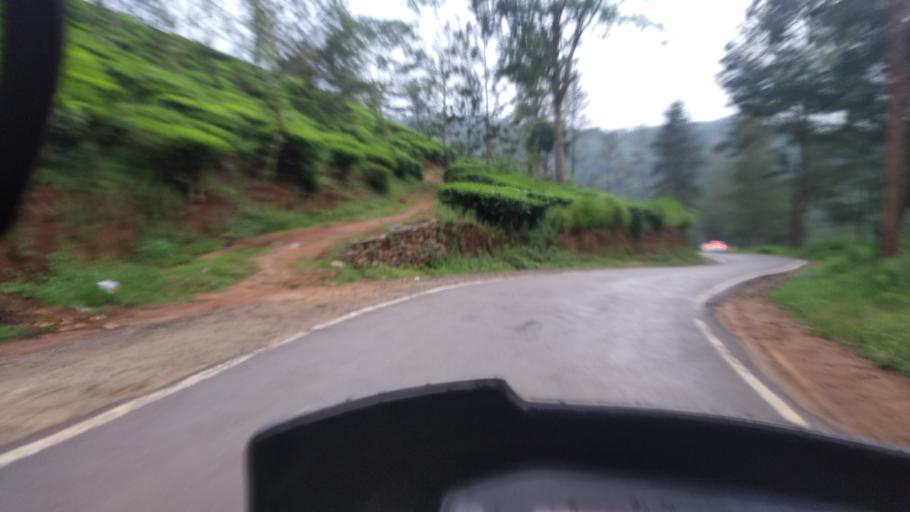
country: IN
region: Tamil Nadu
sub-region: Theni
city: Gudalur
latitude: 9.5680
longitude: 77.0815
